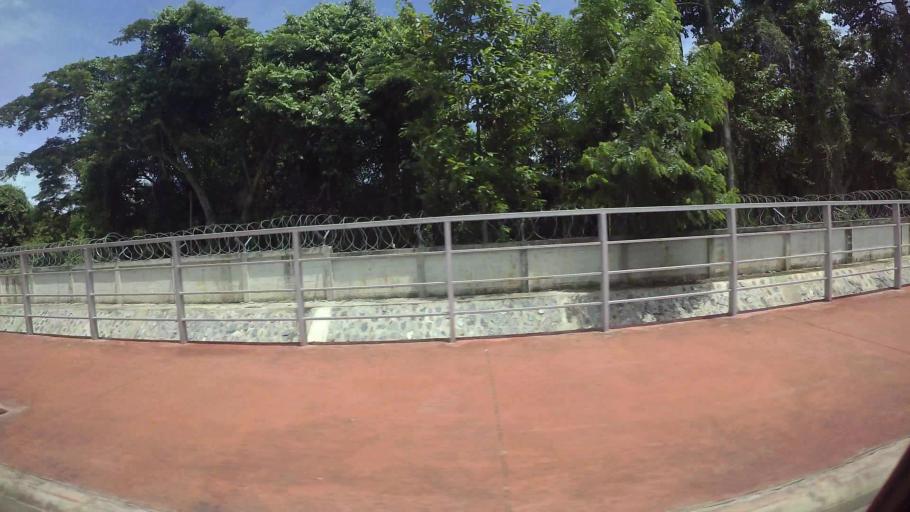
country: TH
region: Chon Buri
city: Sattahip
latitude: 12.7125
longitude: 100.8861
